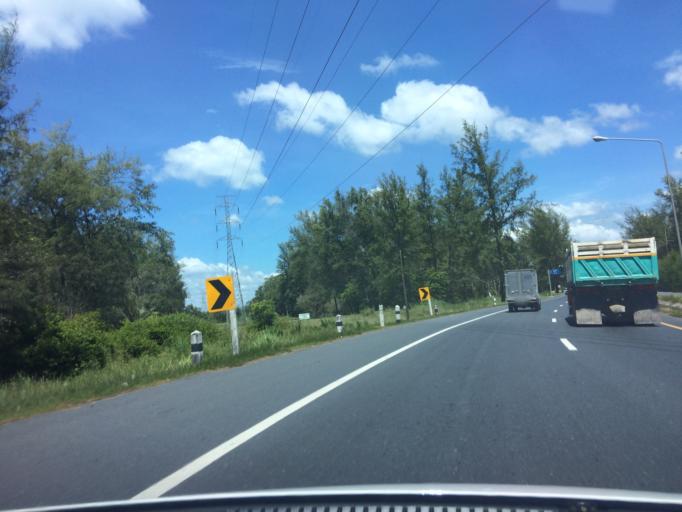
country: TH
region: Phuket
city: Thalang
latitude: 8.1903
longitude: 98.2879
